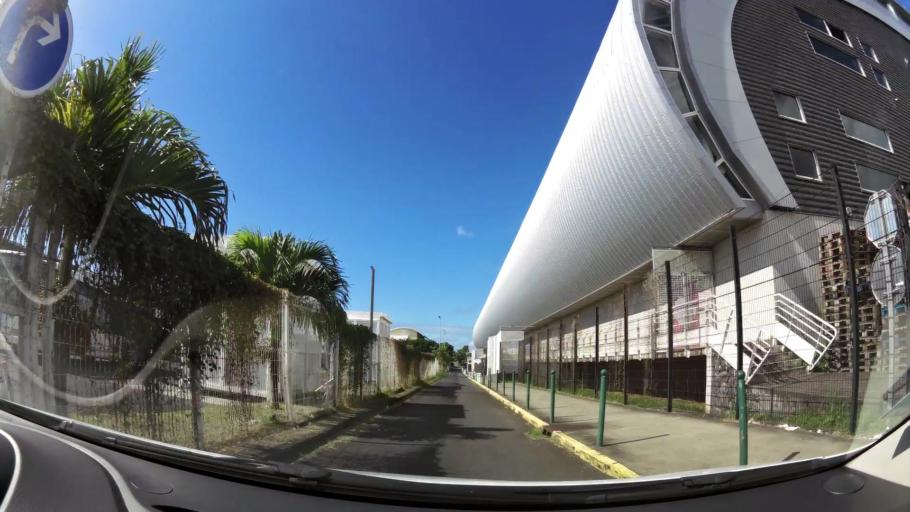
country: RE
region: Reunion
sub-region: Reunion
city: Saint-Denis
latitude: -20.8925
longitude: 55.4971
